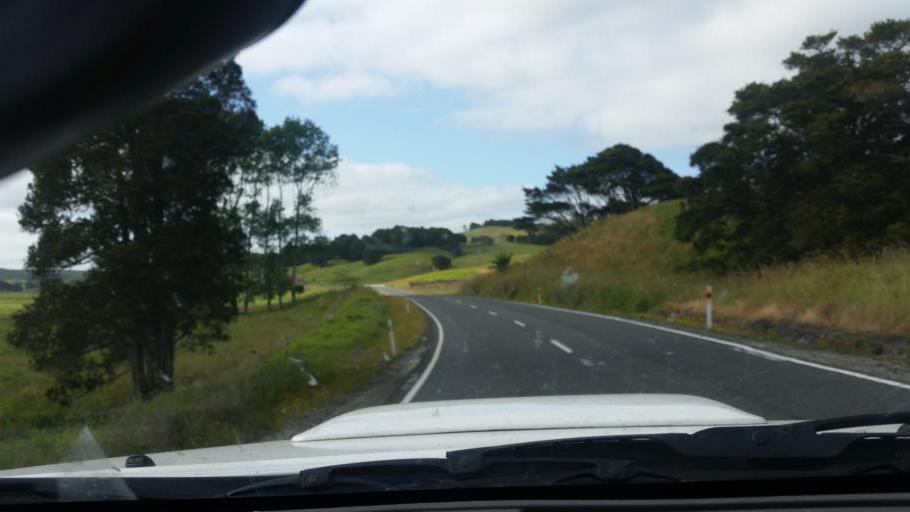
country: NZ
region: Northland
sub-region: Kaipara District
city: Dargaville
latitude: -35.8467
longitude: 173.8434
